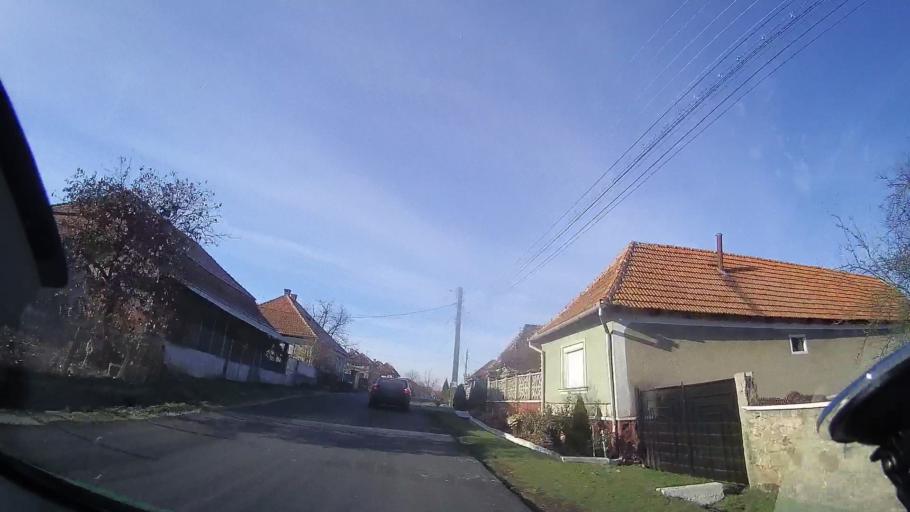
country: RO
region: Bihor
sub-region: Comuna Magesti
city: Magesti
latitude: 47.0153
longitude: 22.4371
